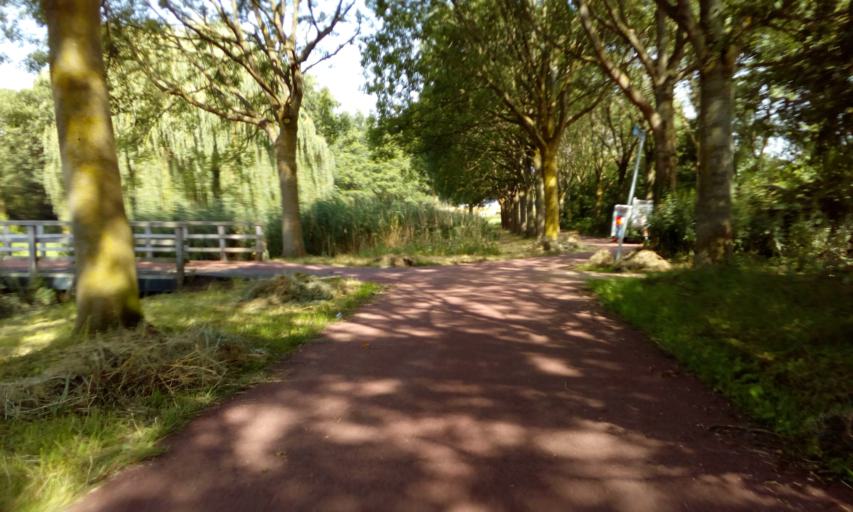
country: NL
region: South Holland
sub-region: Gemeente Lansingerland
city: Bergschenhoek
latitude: 51.9660
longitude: 4.5364
